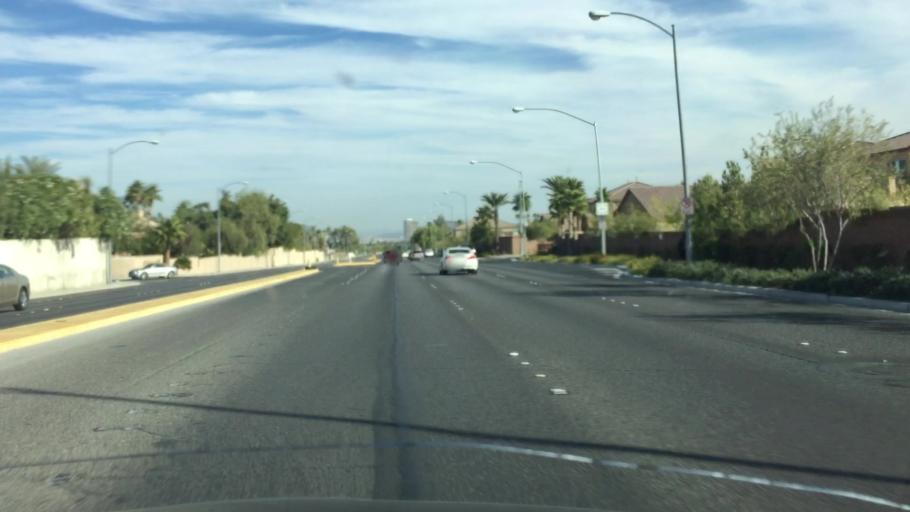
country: US
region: Nevada
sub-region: Clark County
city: Spring Valley
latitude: 36.1293
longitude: -115.2505
